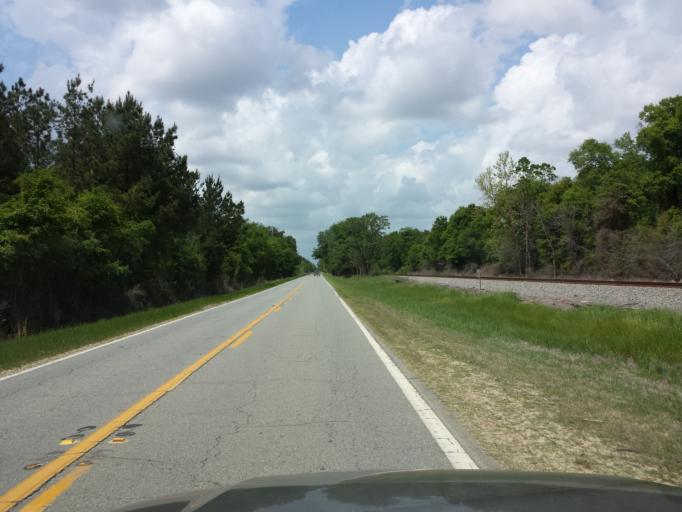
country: US
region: Georgia
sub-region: Echols County
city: Statenville
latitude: 30.6433
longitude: -83.1378
